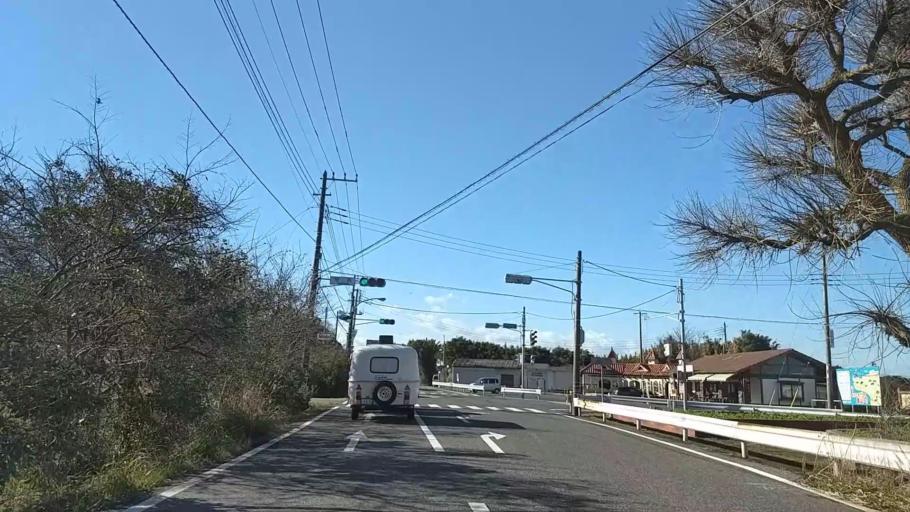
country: JP
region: Chiba
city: Tateyama
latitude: 34.9250
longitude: 139.8321
